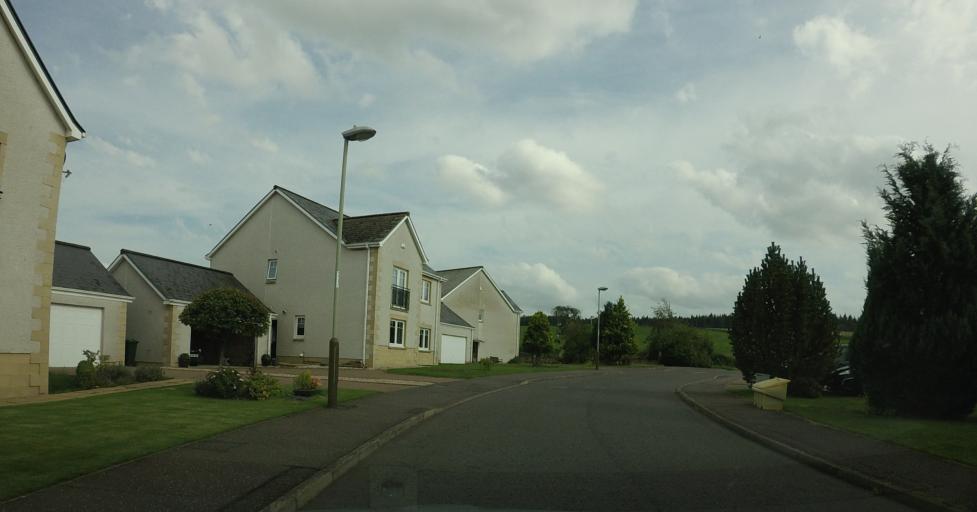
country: GB
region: Scotland
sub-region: Perth and Kinross
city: Methven
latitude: 56.3849
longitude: -3.6323
